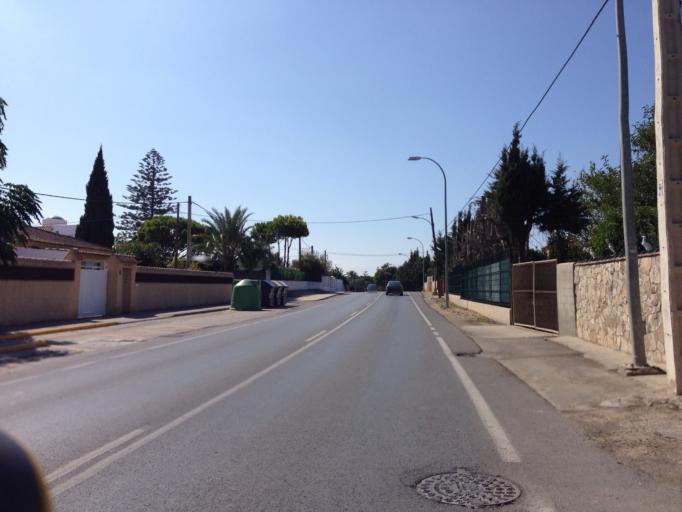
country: ES
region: Andalusia
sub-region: Provincia de Cadiz
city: Chiclana de la Frontera
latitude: 36.4092
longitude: -6.1599
